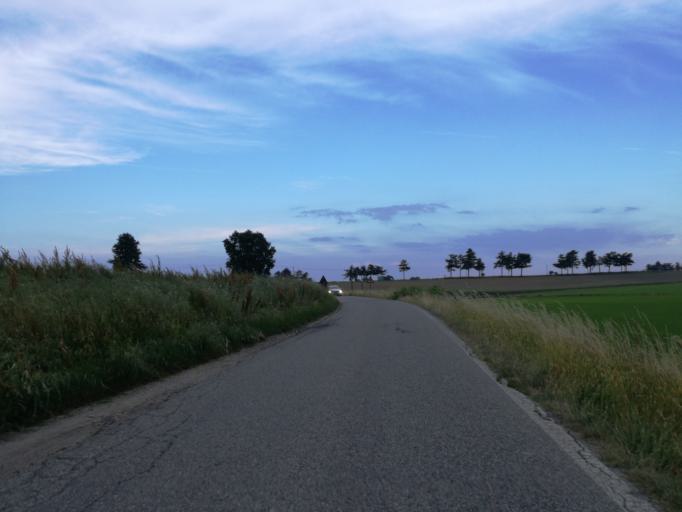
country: IT
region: Piedmont
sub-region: Provincia di Novara
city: Lumellogno
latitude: 45.3802
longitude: 8.6138
